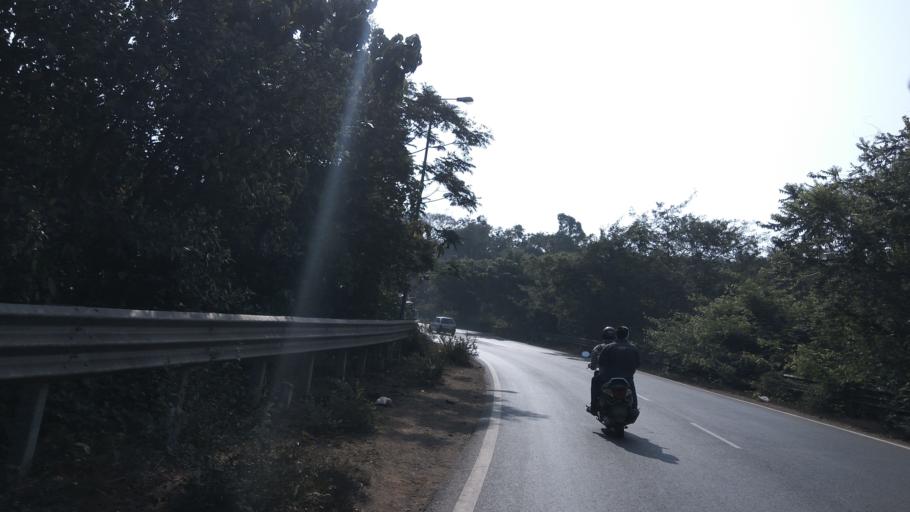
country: IN
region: Goa
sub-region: North Goa
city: Bandora
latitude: 15.4377
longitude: 73.9770
